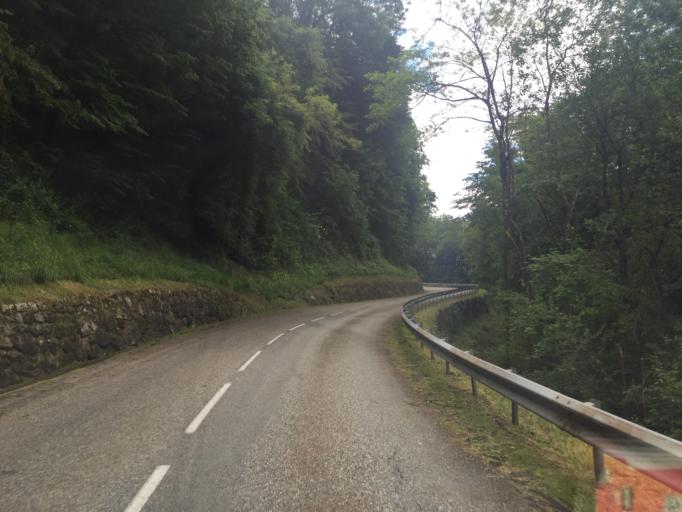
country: FR
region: Rhone-Alpes
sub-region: Departement de la Savoie
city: Barby
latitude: 45.5915
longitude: 6.0220
